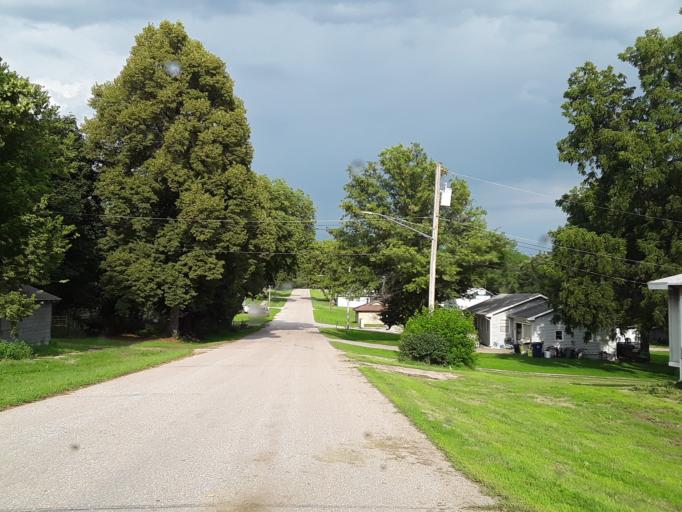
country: US
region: Nebraska
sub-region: Saunders County
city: Ashland
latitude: 41.0951
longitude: -96.4352
